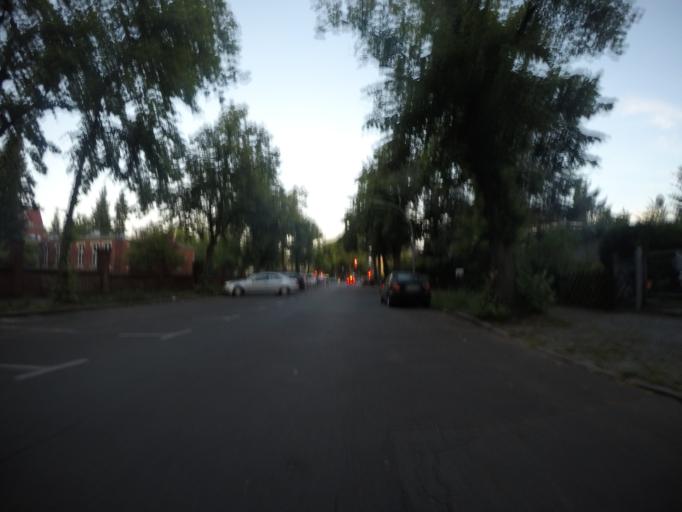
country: DE
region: Berlin
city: Dahlem
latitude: 52.4486
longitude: 13.2985
